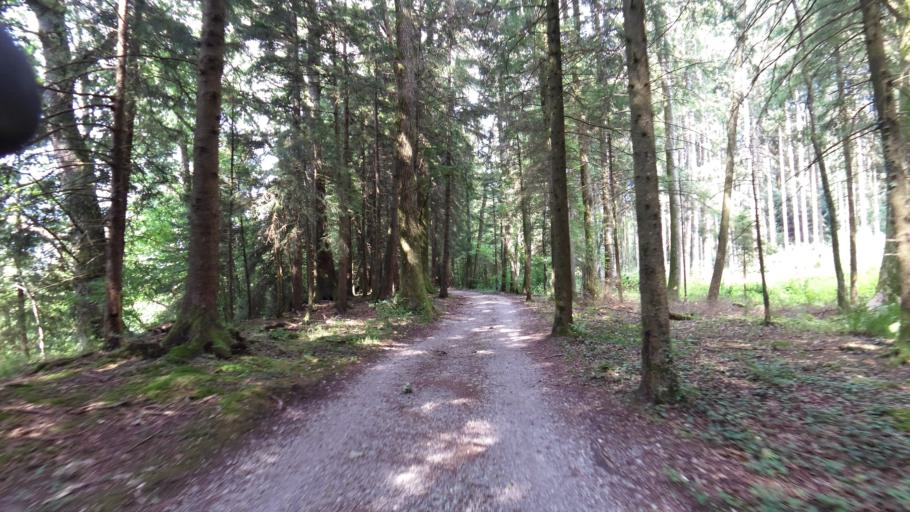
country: DE
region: Bavaria
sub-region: Upper Bavaria
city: Chieming
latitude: 47.8696
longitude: 12.5212
